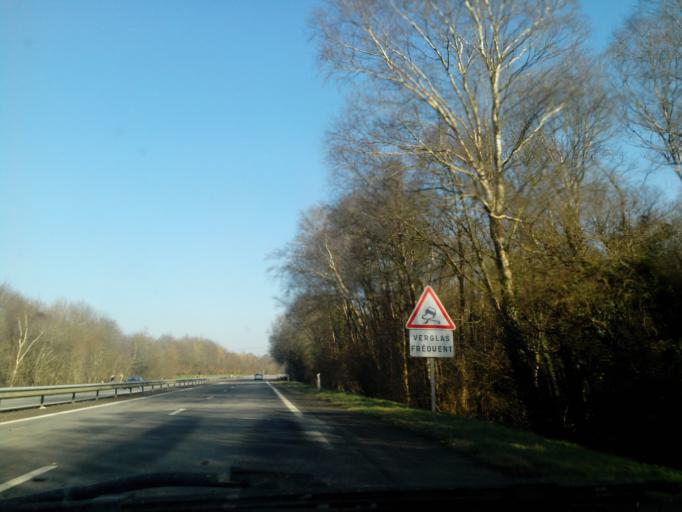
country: FR
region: Brittany
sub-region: Departement du Morbihan
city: Meneac
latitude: 48.1961
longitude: -2.5027
